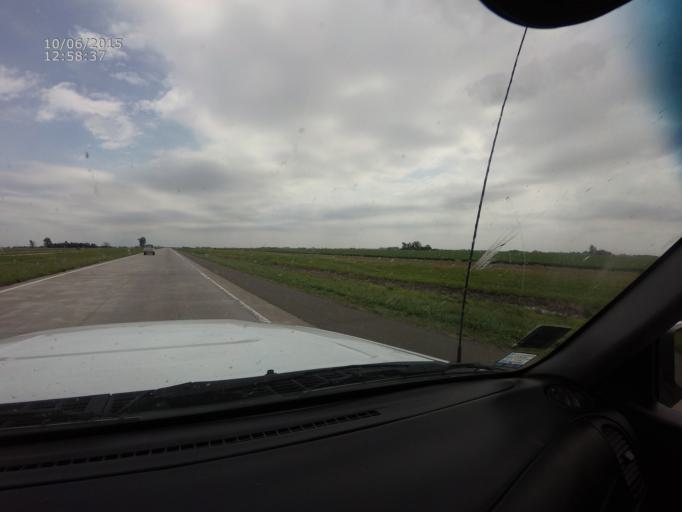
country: AR
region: Santa Fe
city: Armstrong
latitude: -32.8001
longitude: -61.6601
